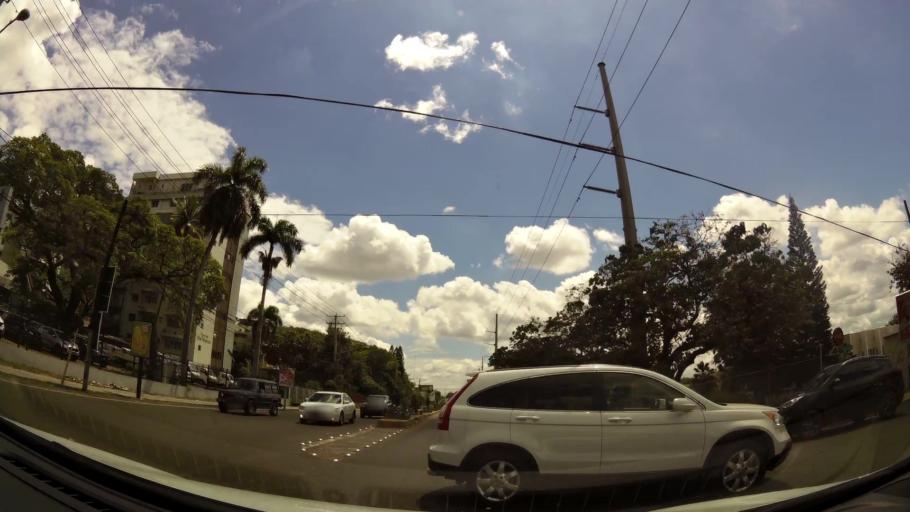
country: DO
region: Santiago
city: Santiago de los Caballeros
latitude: 19.4651
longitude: -70.6867
